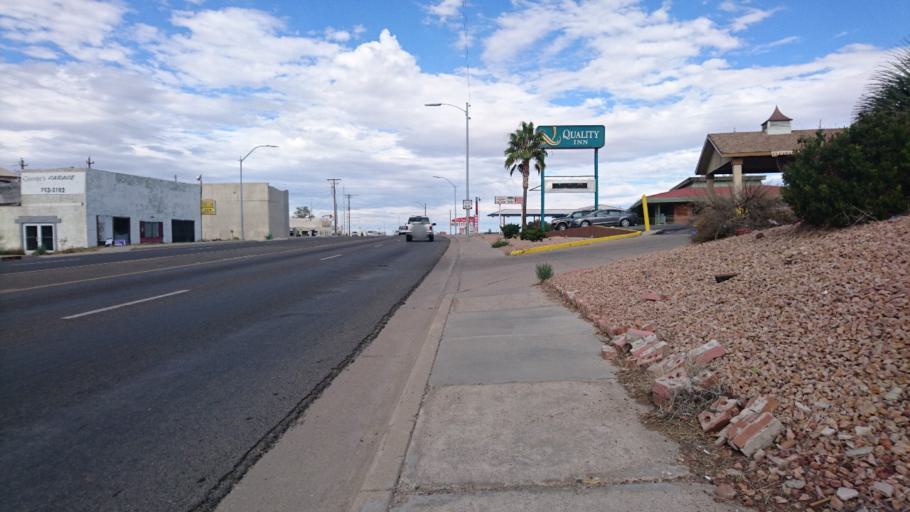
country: US
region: Arizona
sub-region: Mohave County
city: Kingman
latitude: 35.1903
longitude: -114.0354
